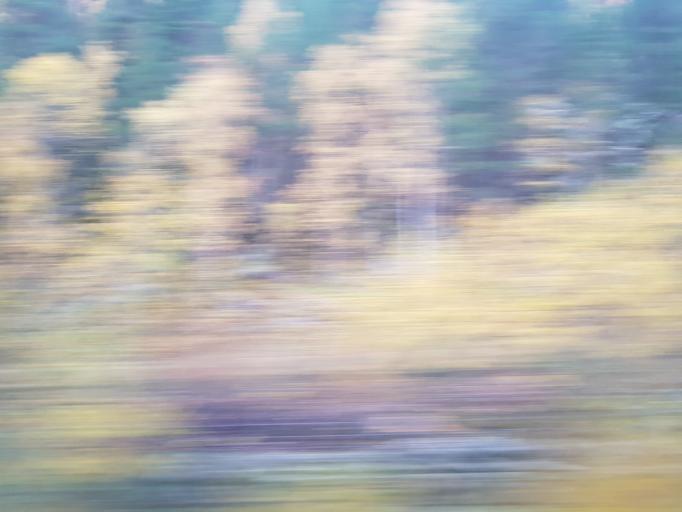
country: NO
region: Oppland
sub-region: Sel
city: Otta
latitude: 61.8396
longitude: 9.4541
